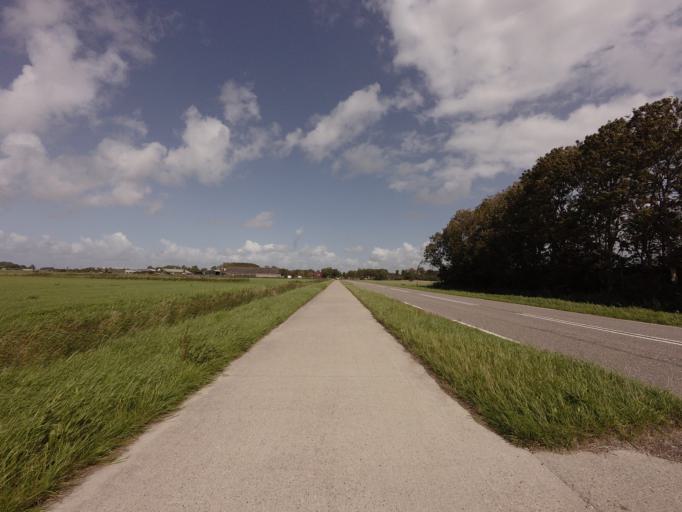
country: NL
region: Friesland
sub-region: Gemeente Harlingen
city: Harlingen
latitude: 53.1448
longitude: 5.4782
